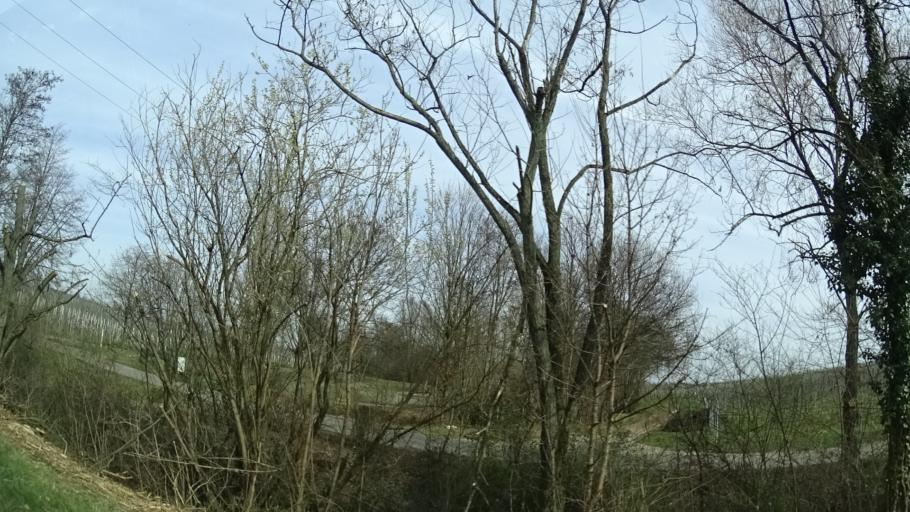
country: DE
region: Rheinland-Pfalz
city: Sankt Martin
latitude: 49.2984
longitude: 8.1105
